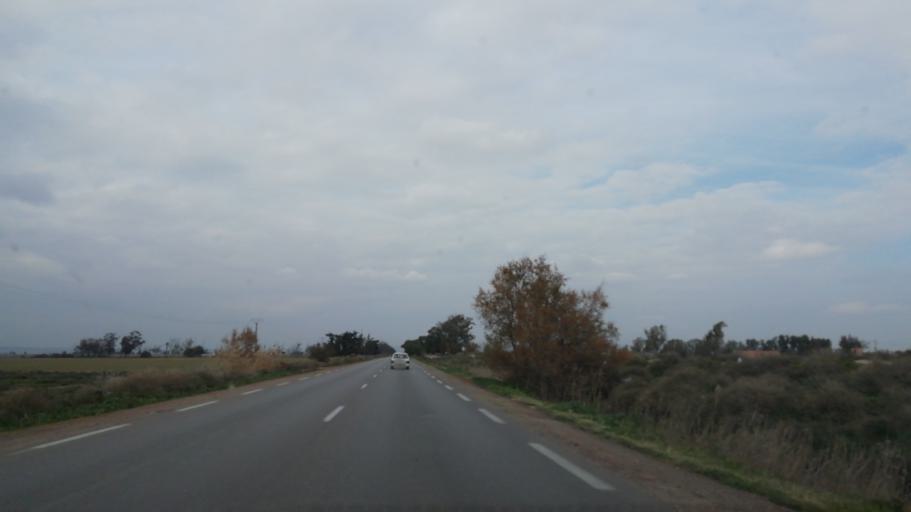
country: DZ
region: Mostaganem
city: Mostaganem
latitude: 35.6690
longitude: 0.0579
